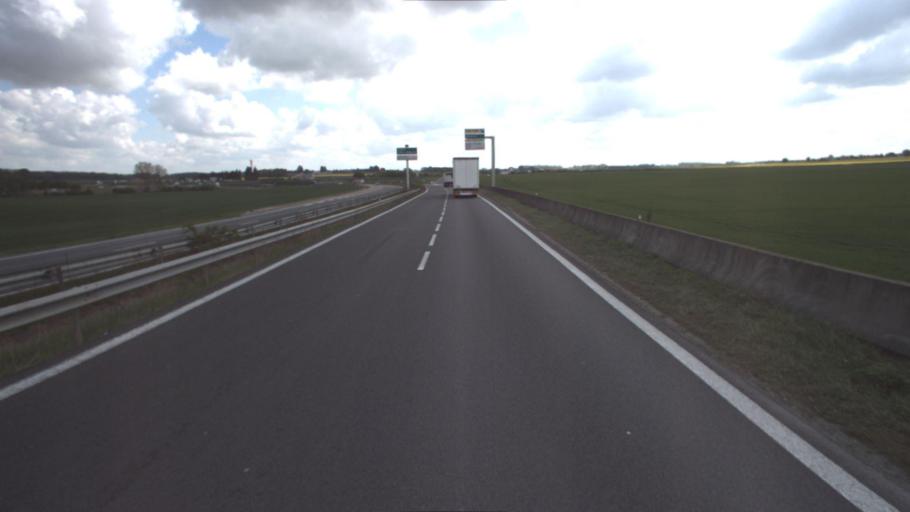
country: FR
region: Ile-de-France
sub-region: Departement de Seine-et-Marne
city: Jouy-le-Chatel
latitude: 48.6841
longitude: 3.0959
